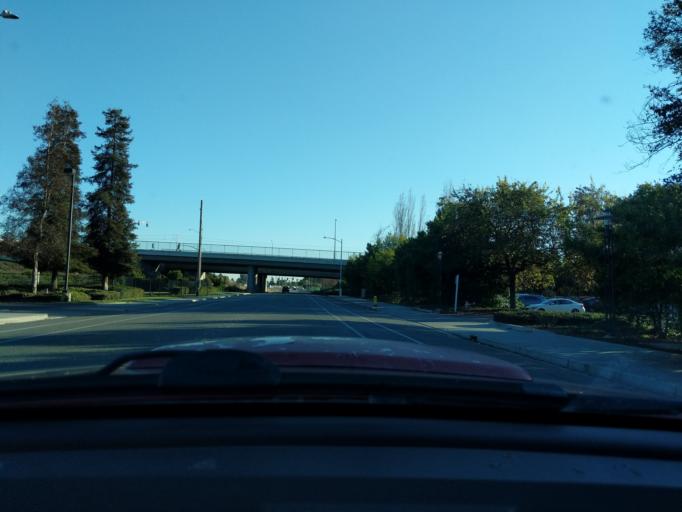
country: US
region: California
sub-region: Santa Clara County
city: Milpitas
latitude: 37.4164
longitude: -121.9148
